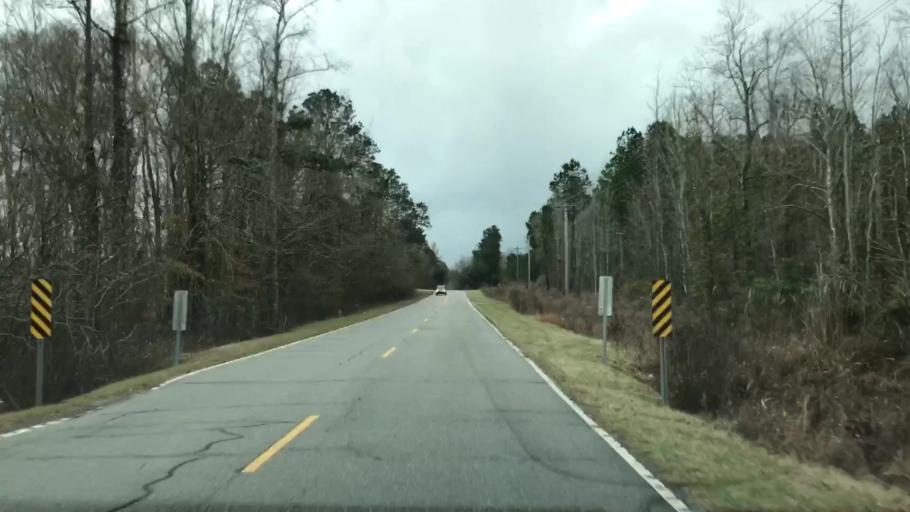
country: US
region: South Carolina
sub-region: Florence County
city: Johnsonville
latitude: 33.6631
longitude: -79.4097
